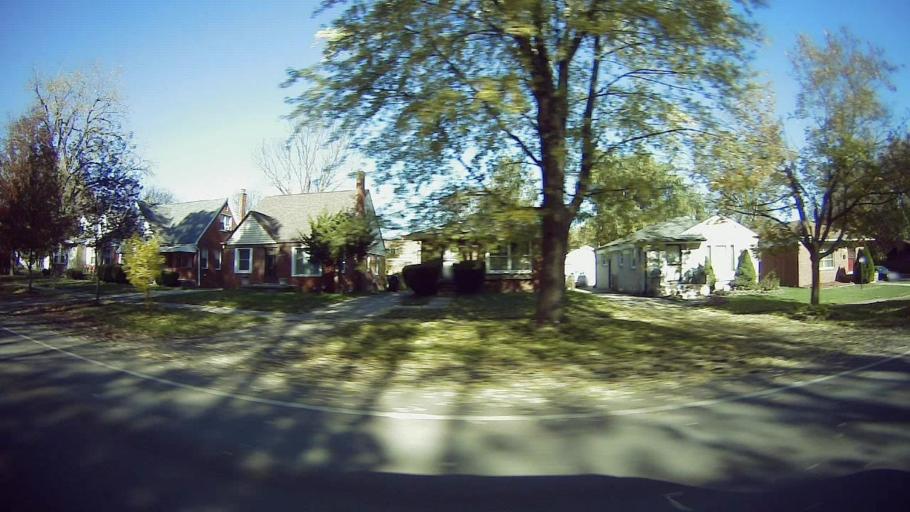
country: US
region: Michigan
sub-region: Wayne County
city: Dearborn Heights
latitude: 42.3643
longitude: -83.2634
